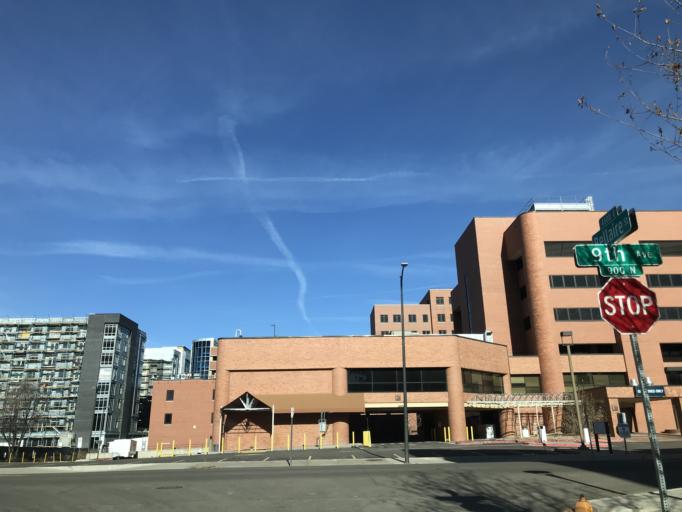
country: US
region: Colorado
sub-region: Arapahoe County
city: Glendale
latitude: 39.7309
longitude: -104.9369
